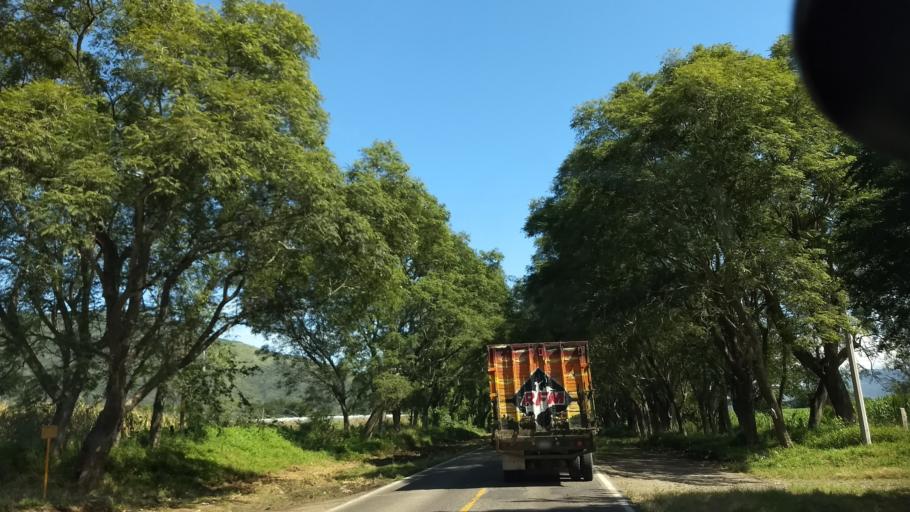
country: MX
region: Jalisco
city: Tuxpan
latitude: 19.5338
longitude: -103.4161
